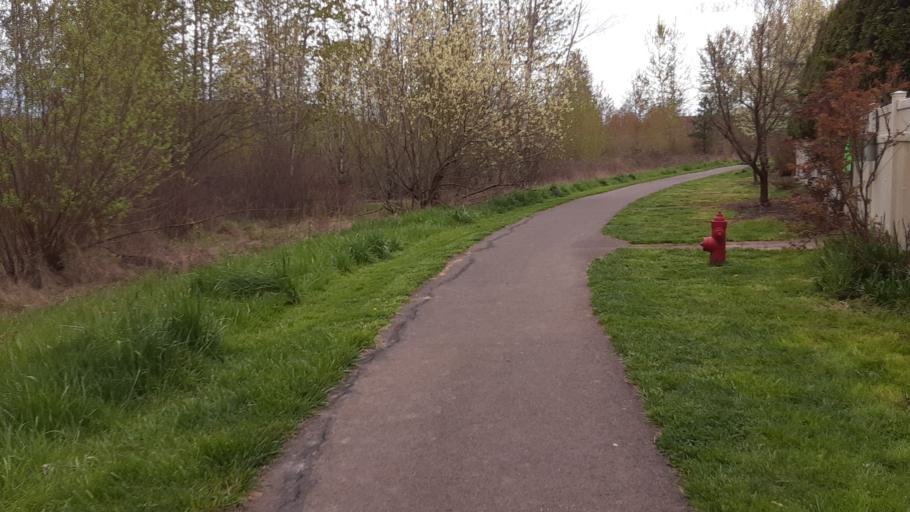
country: US
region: Oregon
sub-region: Benton County
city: Corvallis
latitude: 44.5351
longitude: -123.2583
